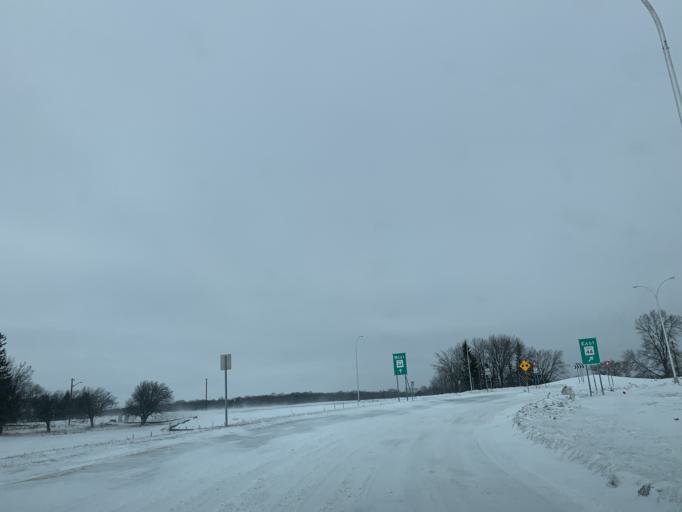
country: US
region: Minnesota
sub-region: Carver County
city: Carver
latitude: 44.7902
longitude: -93.6338
